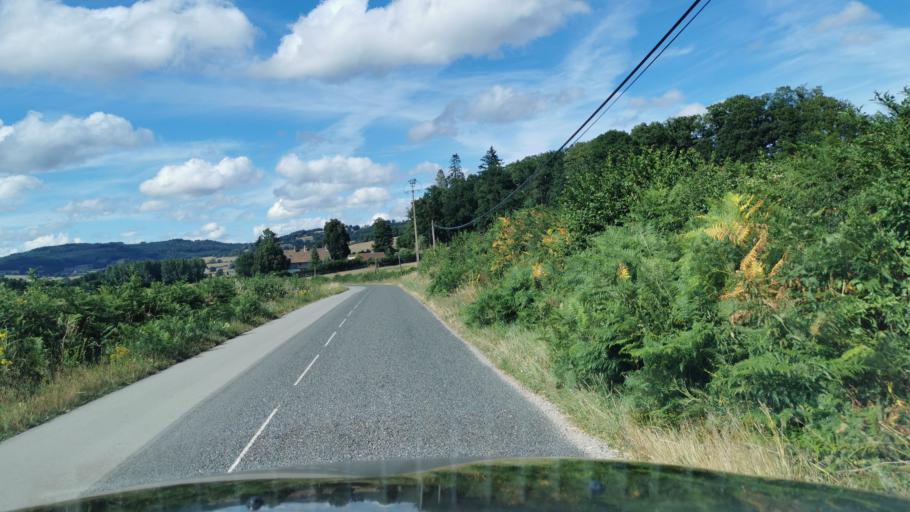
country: FR
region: Bourgogne
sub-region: Departement de Saone-et-Loire
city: Marmagne
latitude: 46.8355
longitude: 4.3184
